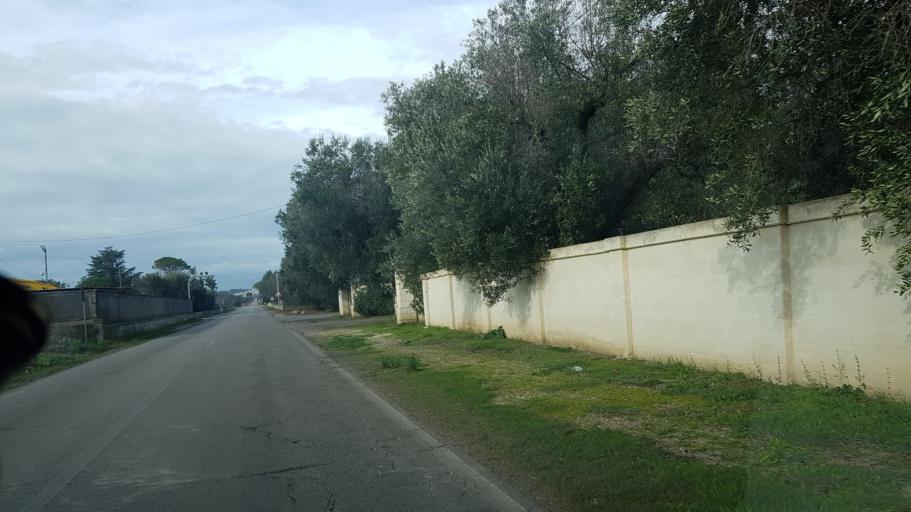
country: IT
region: Apulia
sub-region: Provincia di Brindisi
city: Oria
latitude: 40.4860
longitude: 17.6734
